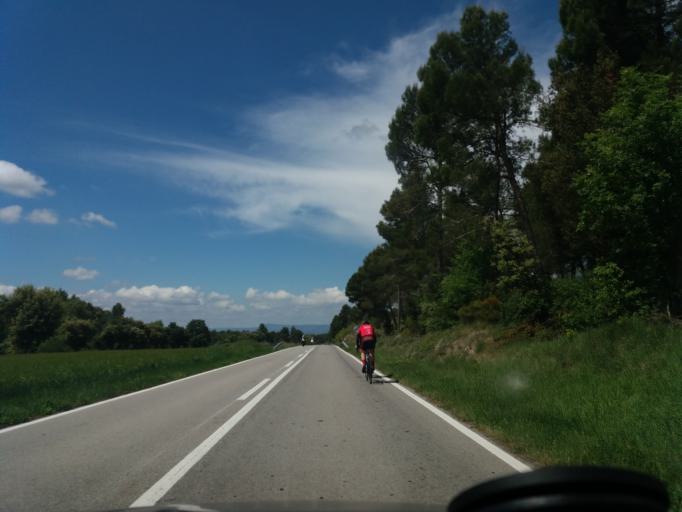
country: ES
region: Catalonia
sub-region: Provincia de Barcelona
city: Artes
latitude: 41.7796
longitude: 1.9778
